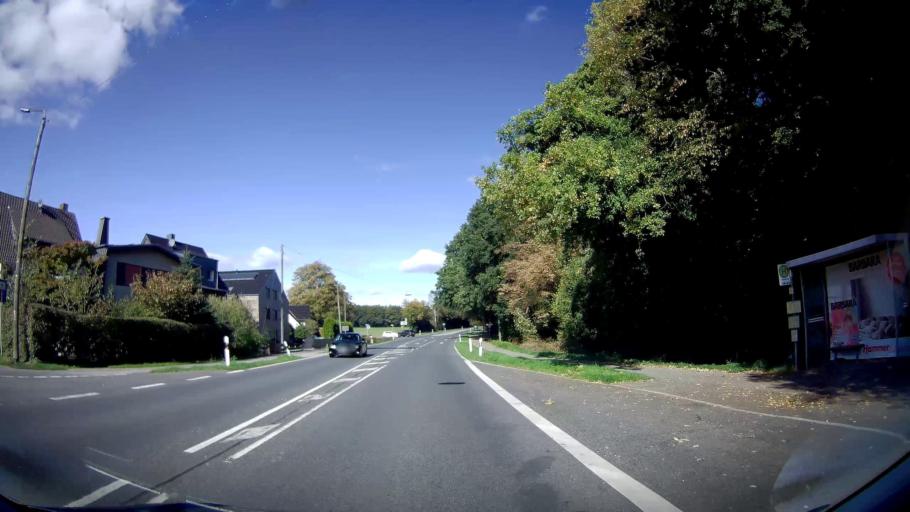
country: DE
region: North Rhine-Westphalia
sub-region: Regierungsbezirk Dusseldorf
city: Dinslaken
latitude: 51.6033
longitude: 6.7560
